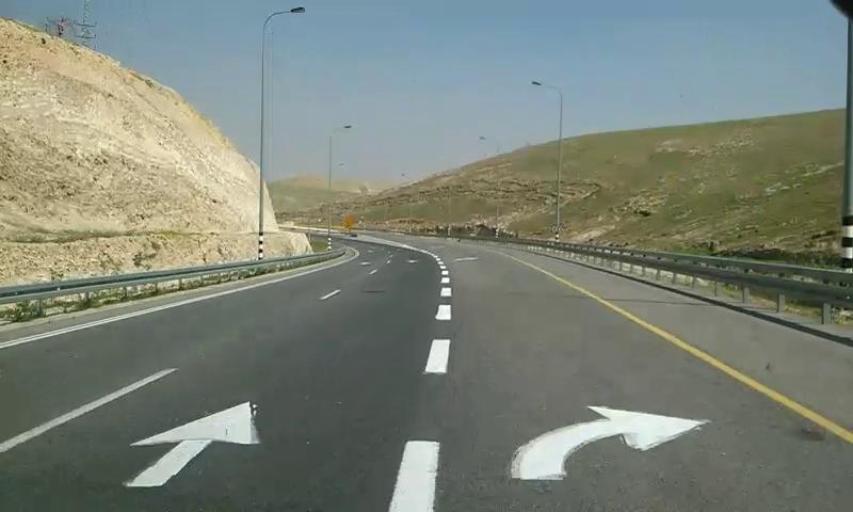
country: PS
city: Az Za`ayyim
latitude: 31.8089
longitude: 35.3375
